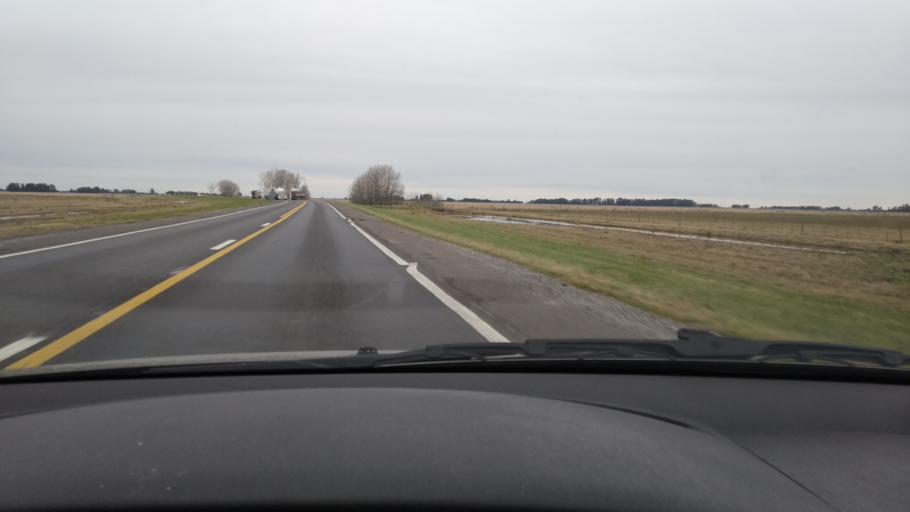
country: AR
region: Buenos Aires
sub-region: Partido de Las Flores
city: Las Flores
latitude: -36.1644
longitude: -59.2271
